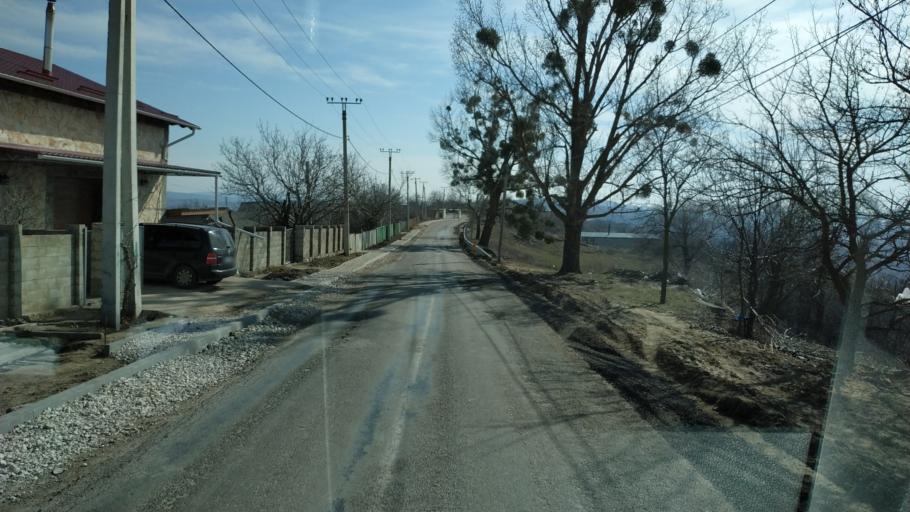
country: MD
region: Nisporeni
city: Nisporeni
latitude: 47.2078
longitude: 28.0580
